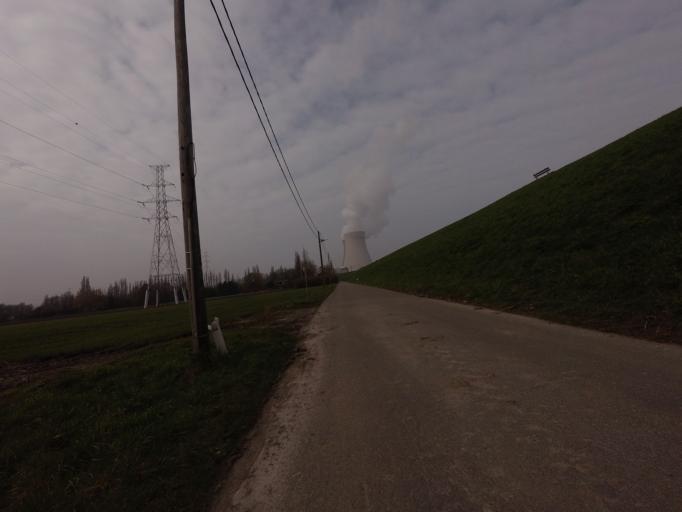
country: BE
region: Flanders
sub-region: Provincie Oost-Vlaanderen
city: Beveren
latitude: 51.3150
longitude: 4.2646
